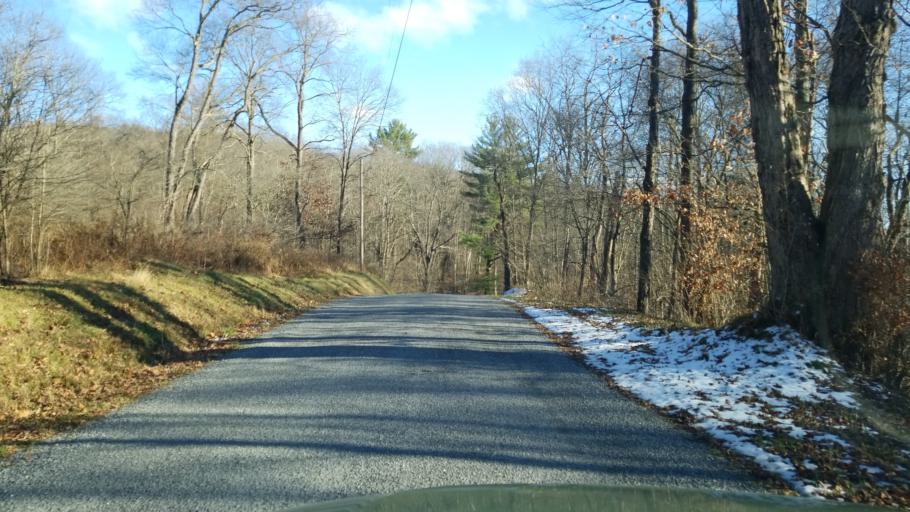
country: US
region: Pennsylvania
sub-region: Jefferson County
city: Brockway
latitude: 41.2786
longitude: -78.8182
